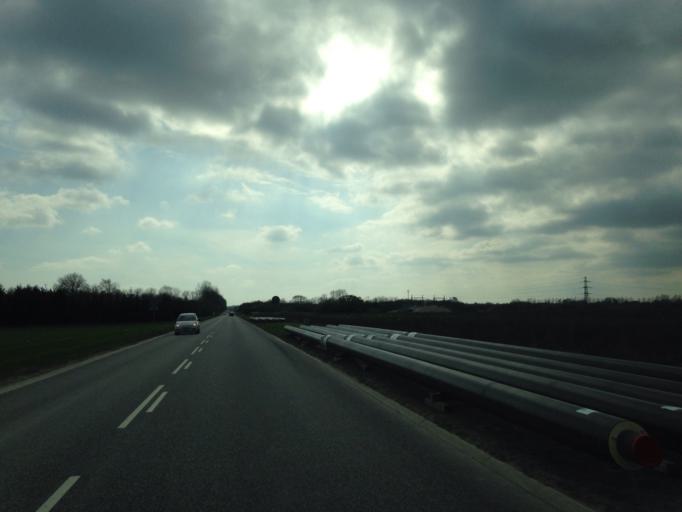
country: DK
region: Zealand
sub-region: Greve Kommune
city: Greve
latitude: 55.6145
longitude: 12.3116
